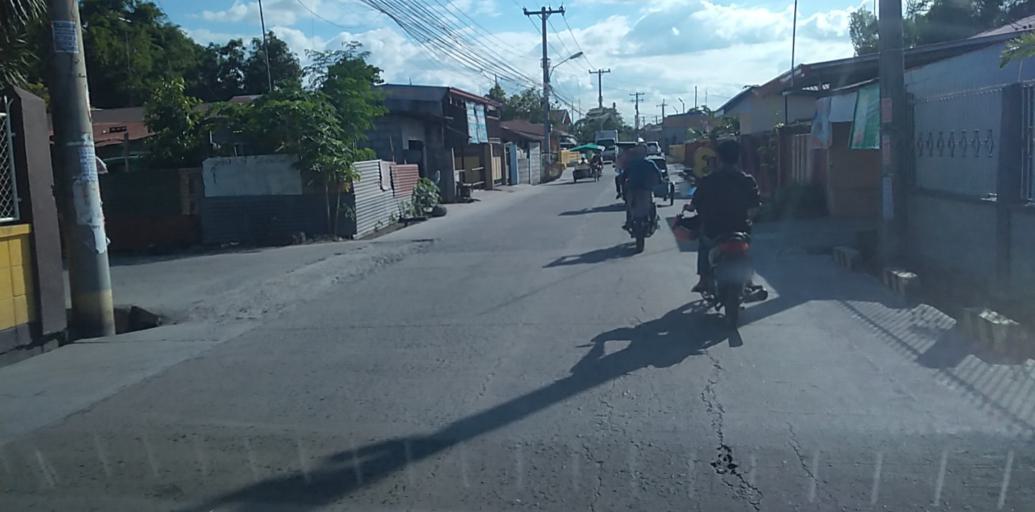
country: PH
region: Central Luzon
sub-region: Province of Pampanga
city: Acli
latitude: 15.1153
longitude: 120.6339
